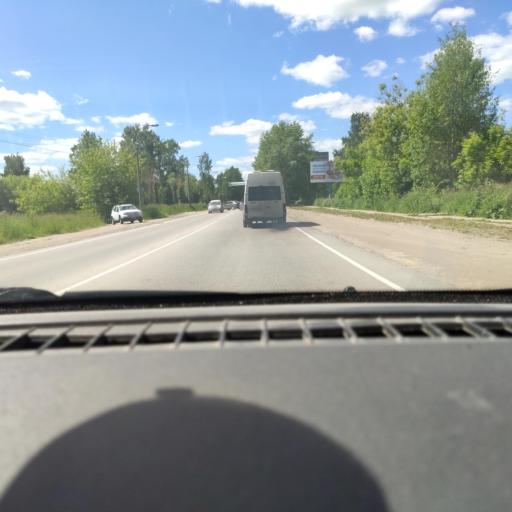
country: RU
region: Perm
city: Krasnokamsk
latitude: 58.0767
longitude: 55.7207
